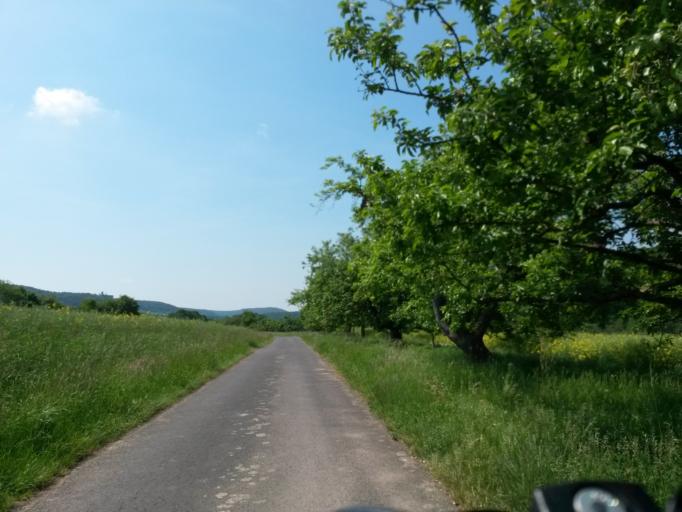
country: DE
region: Bavaria
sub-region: Regierungsbezirk Unterfranken
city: Euerdorf
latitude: 50.1531
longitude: 9.9930
